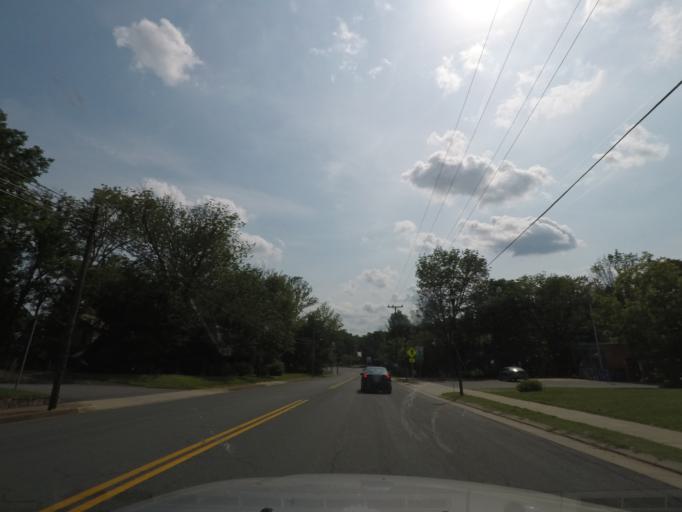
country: US
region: Virginia
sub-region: Fluvanna County
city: Weber City
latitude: 37.7644
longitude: -78.2609
